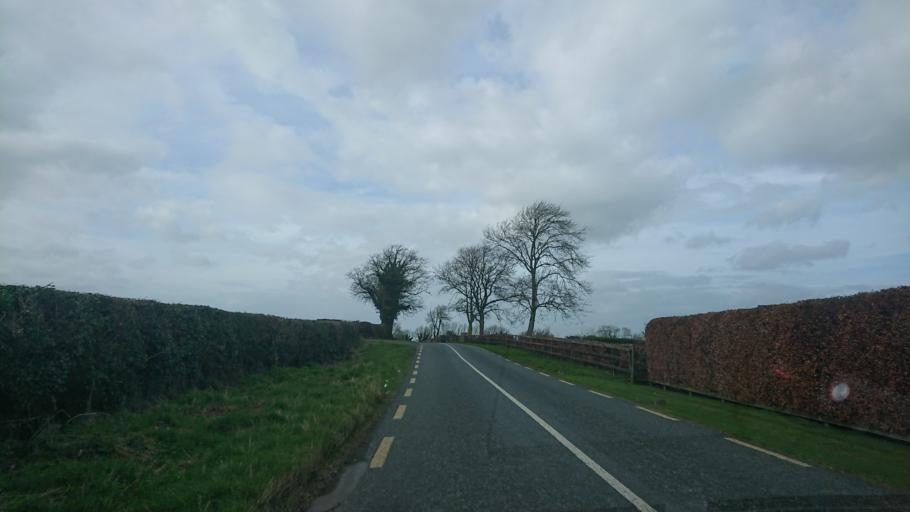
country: IE
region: Leinster
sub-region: Kildare
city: Naas
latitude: 53.1920
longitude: -6.6475
